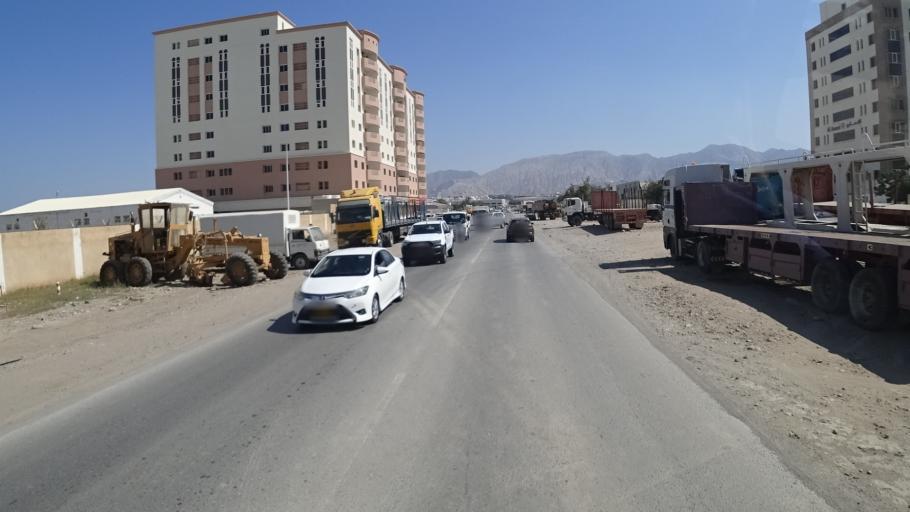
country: OM
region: Muhafazat Masqat
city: Bawshar
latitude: 23.5734
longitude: 58.3749
